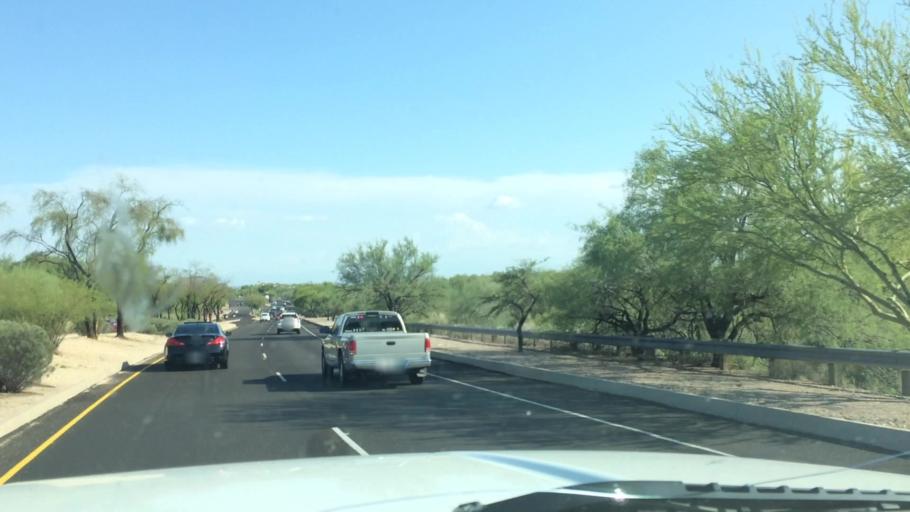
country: US
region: Arizona
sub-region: Pima County
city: Catalina Foothills
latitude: 32.3163
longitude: -110.9135
